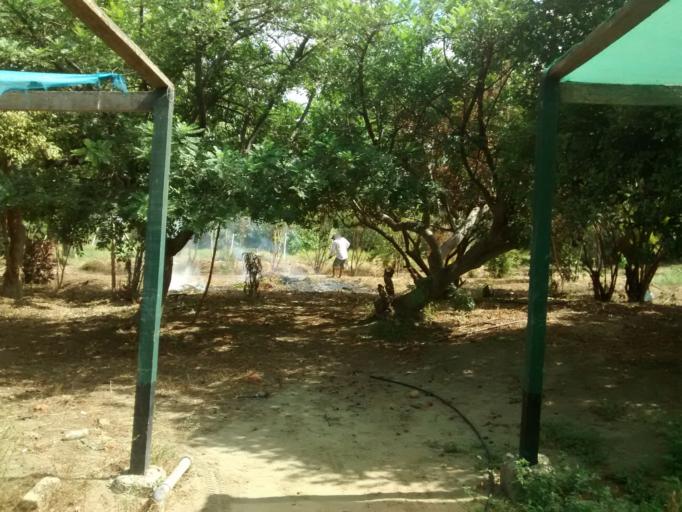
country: PE
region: Piura
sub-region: Provincia de Piura
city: Piura
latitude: -5.1791
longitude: -80.6165
